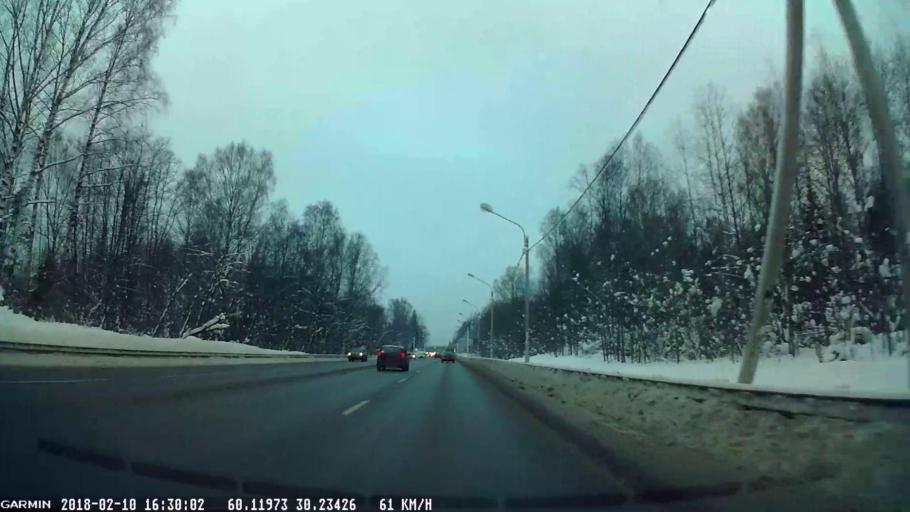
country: RU
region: St.-Petersburg
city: Levashovo
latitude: 60.1204
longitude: 30.2336
